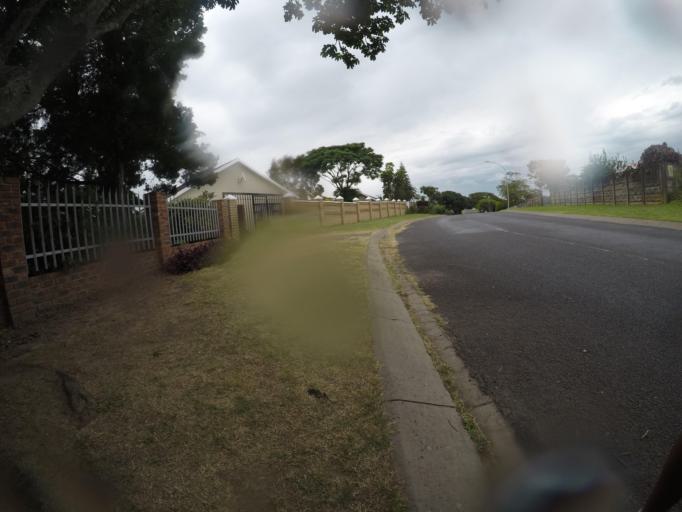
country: ZA
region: Eastern Cape
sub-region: Buffalo City Metropolitan Municipality
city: East London
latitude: -32.9939
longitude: 27.8504
